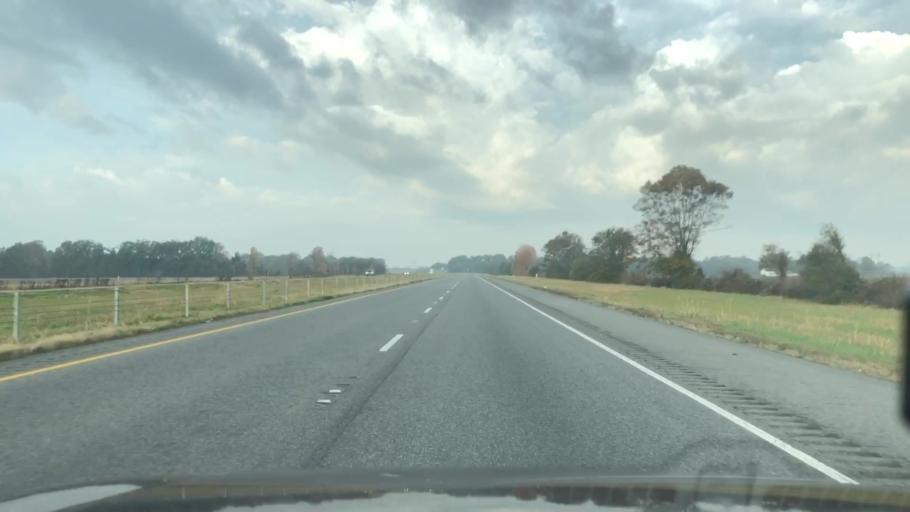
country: US
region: Louisiana
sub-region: Madison Parish
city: Tallulah
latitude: 32.4180
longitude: -91.2865
